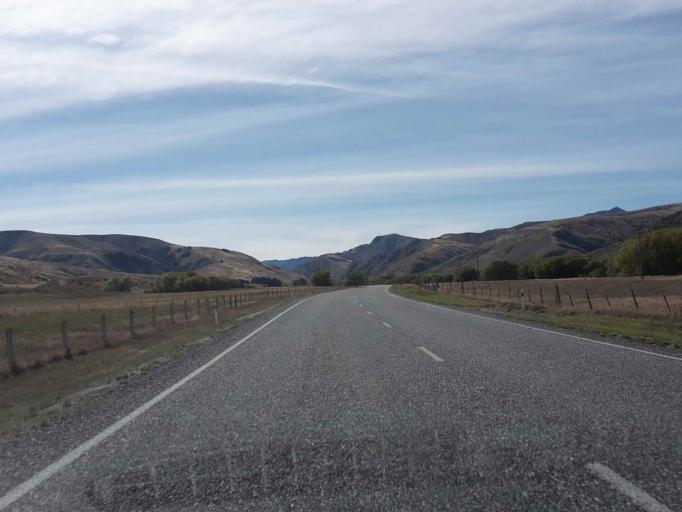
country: NZ
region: Otago
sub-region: Queenstown-Lakes District
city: Wanaka
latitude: -44.6690
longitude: 169.4829
